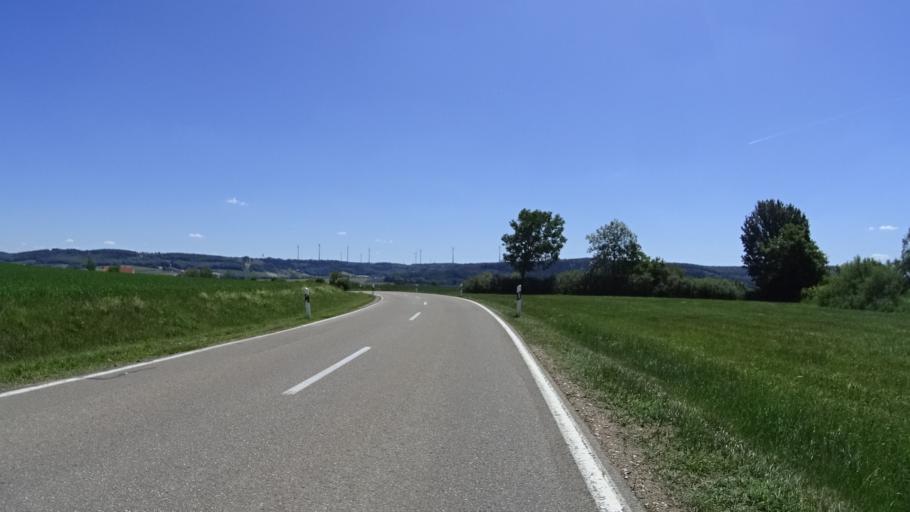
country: DE
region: Bavaria
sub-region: Regierungsbezirk Mittelfranken
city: Hottingen
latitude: 49.0797
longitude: 11.0149
